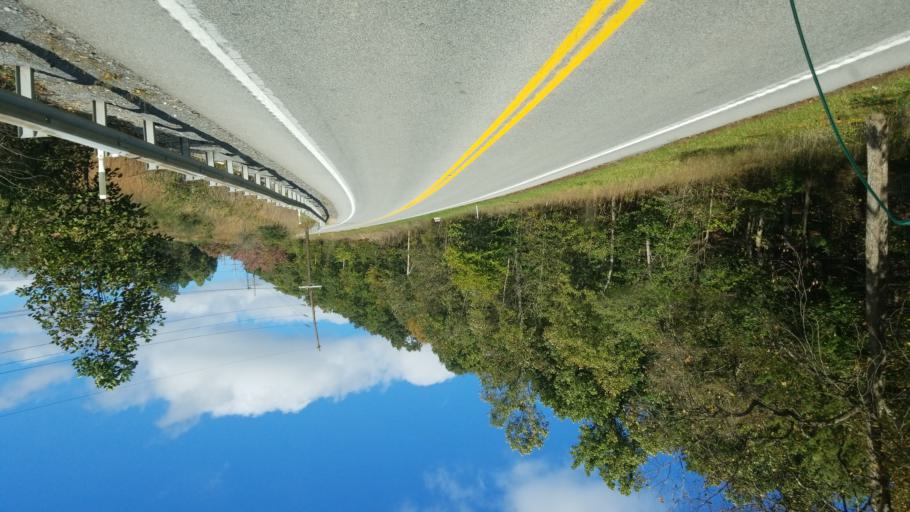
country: US
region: Pennsylvania
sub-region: Fulton County
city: McConnellsburg
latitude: 39.9618
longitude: -78.0254
